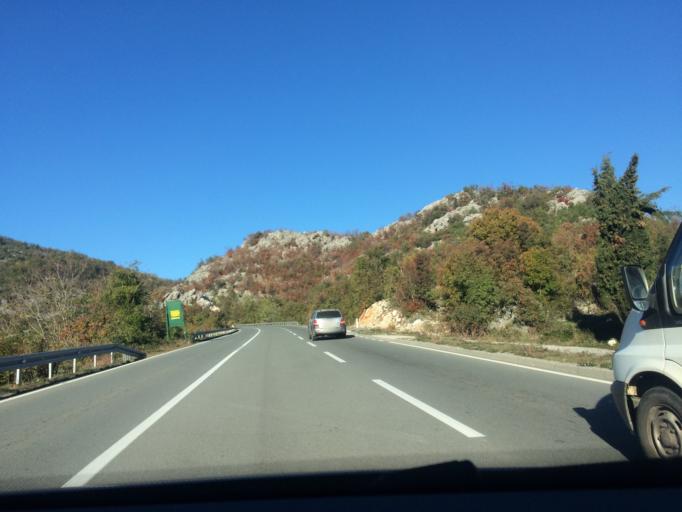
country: ME
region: Cetinje
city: Cetinje
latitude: 42.3780
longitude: 18.9874
